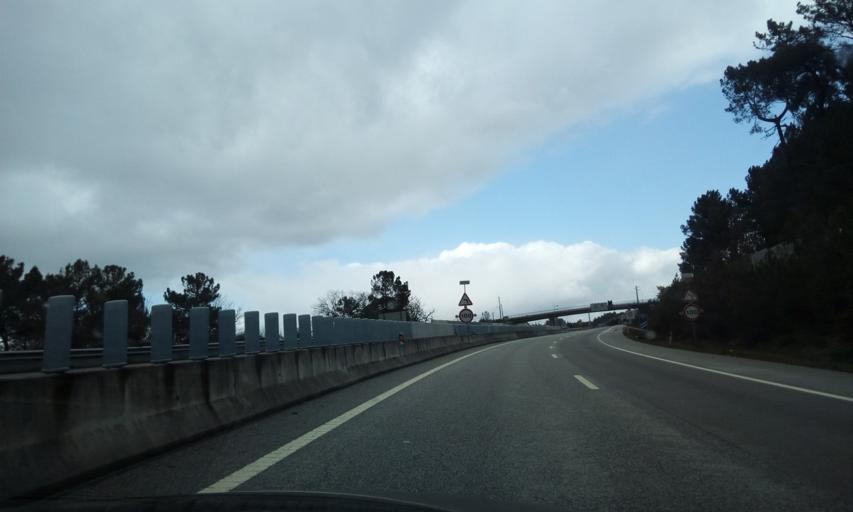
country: PT
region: Viseu
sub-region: Viseu
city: Rio de Loba
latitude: 40.6458
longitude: -7.8607
